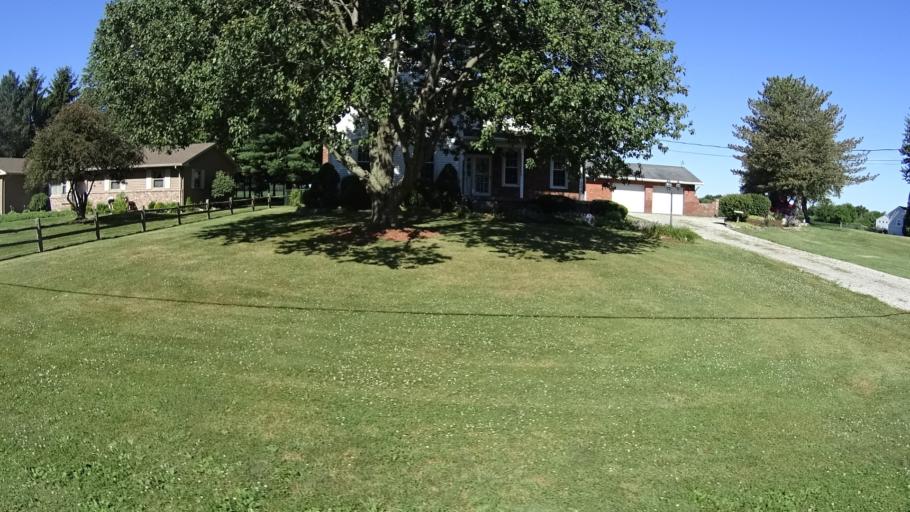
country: US
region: Ohio
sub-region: Erie County
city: Sandusky
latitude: 41.3924
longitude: -82.7106
